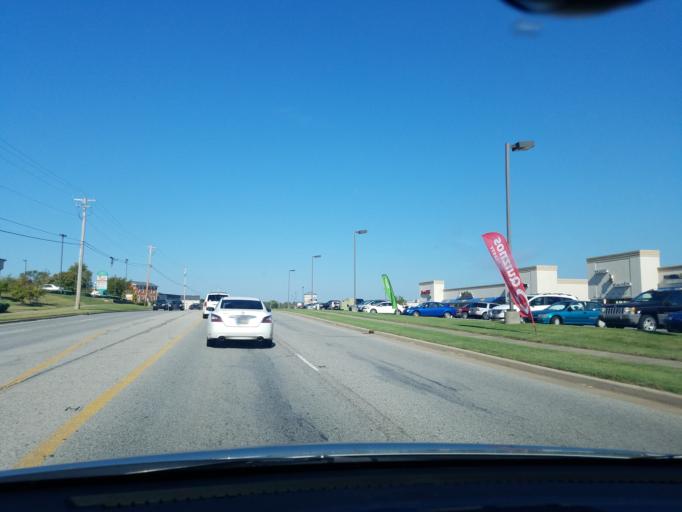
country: US
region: Indiana
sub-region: Clark County
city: Sellersburg
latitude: 38.3502
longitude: -85.7957
